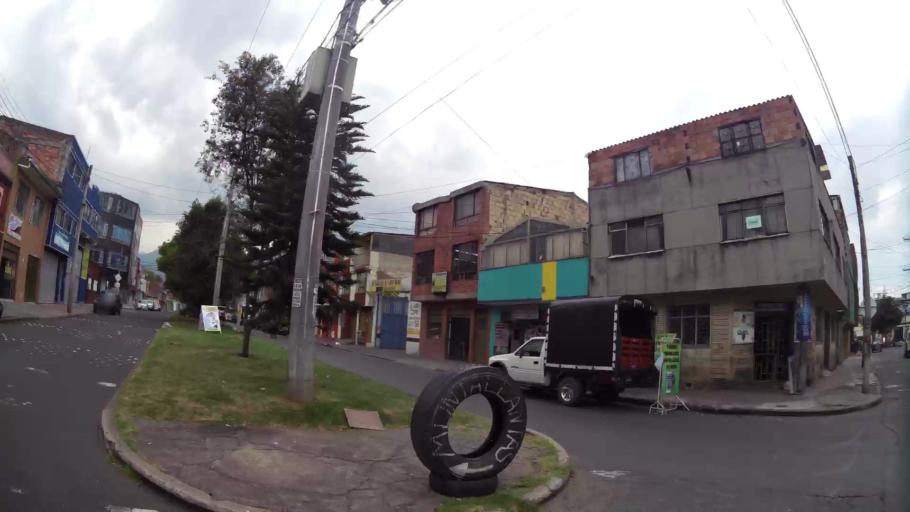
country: CO
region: Bogota D.C.
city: Bogota
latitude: 4.5896
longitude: -74.1032
